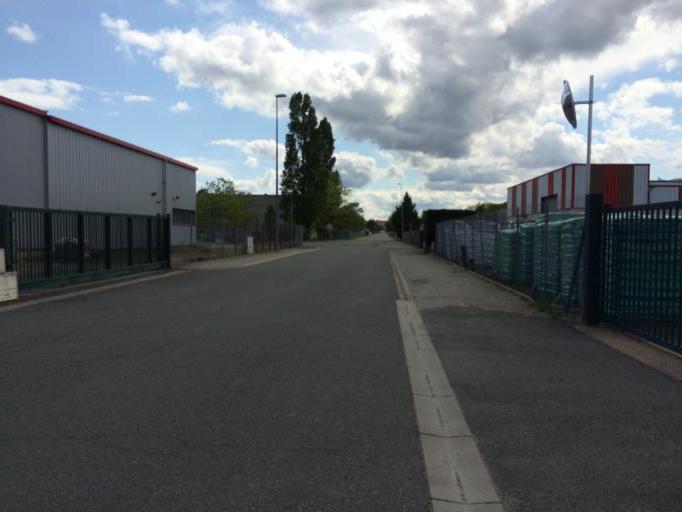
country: FR
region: Rhone-Alpes
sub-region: Departement de l'Ain
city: Saint-Andre-de-Corcy
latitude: 45.9337
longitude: 4.9597
